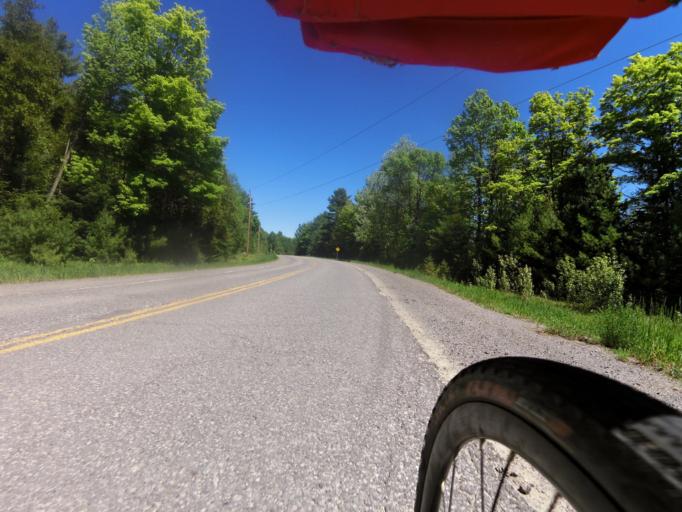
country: CA
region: Ontario
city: Carleton Place
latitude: 45.1854
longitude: -76.3503
